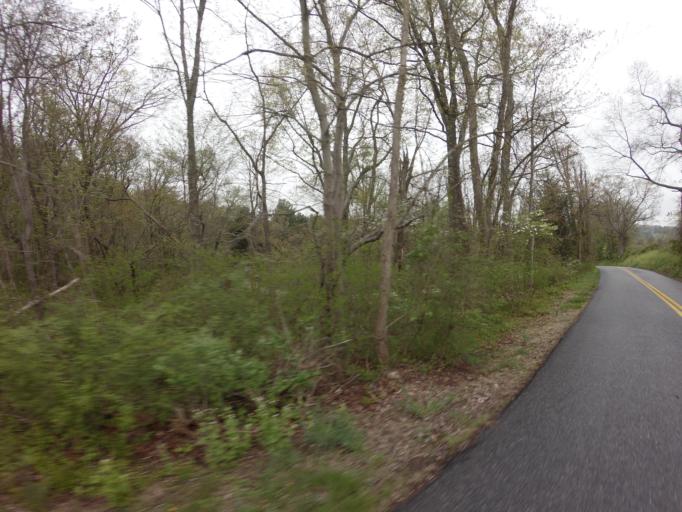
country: US
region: Maryland
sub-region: Baltimore County
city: Hunt Valley
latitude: 39.5723
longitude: -76.7340
